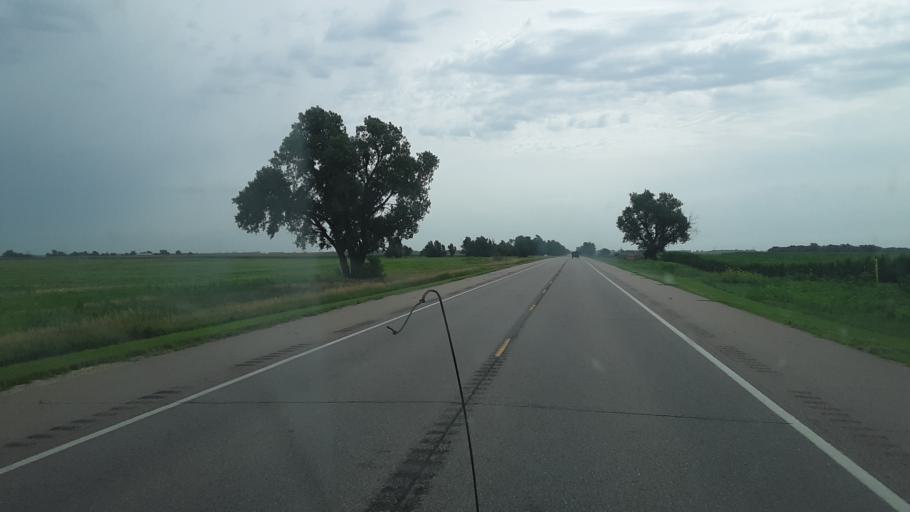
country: US
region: Kansas
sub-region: Stafford County
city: Saint John
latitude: 37.9560
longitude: -98.7804
